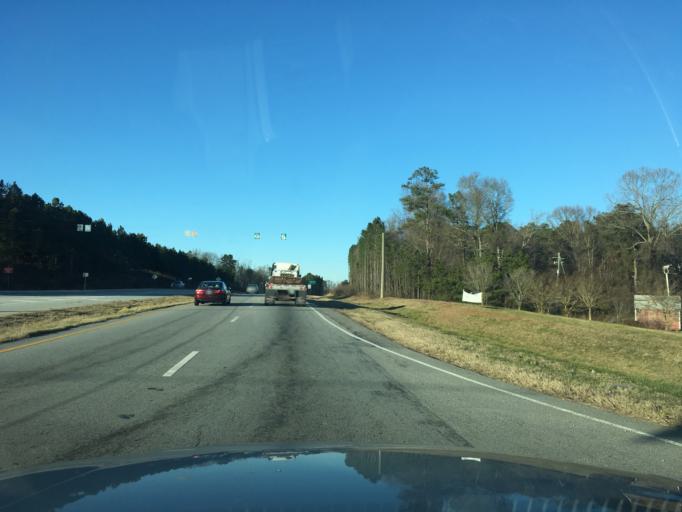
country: US
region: Georgia
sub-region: Carroll County
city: Carrollton
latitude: 33.4602
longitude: -85.1238
